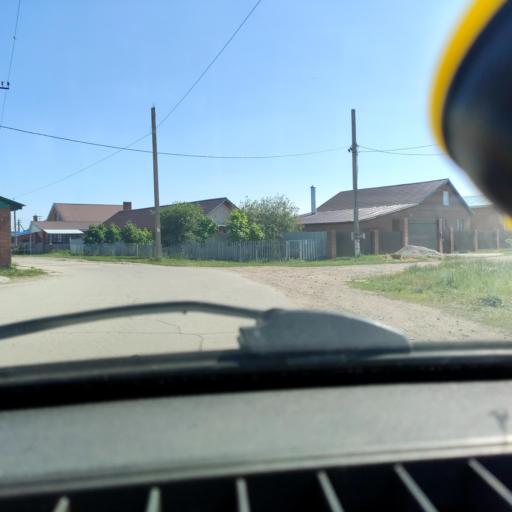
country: RU
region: Samara
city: Povolzhskiy
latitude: 53.6455
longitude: 49.6829
